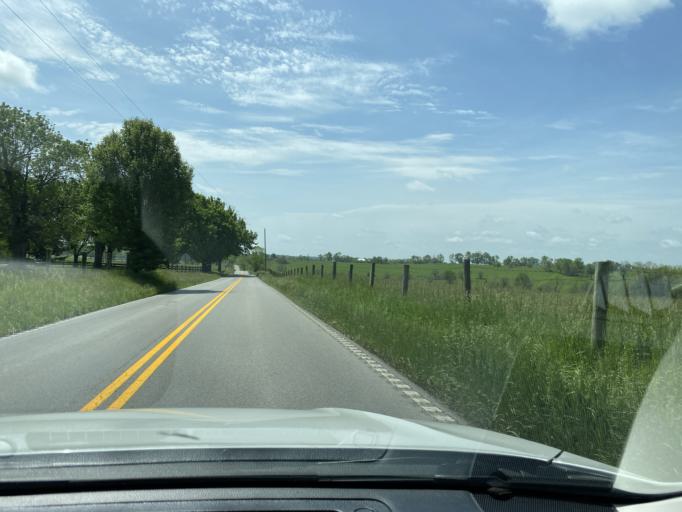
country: US
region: Kentucky
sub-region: Scott County
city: Georgetown
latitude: 38.2525
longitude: -84.5899
